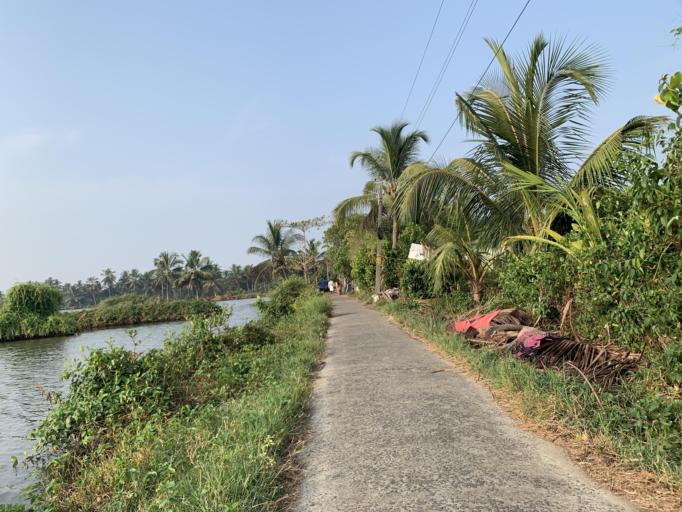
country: IN
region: Kerala
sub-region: Ernakulam
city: Elur
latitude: 10.0180
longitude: 76.2207
